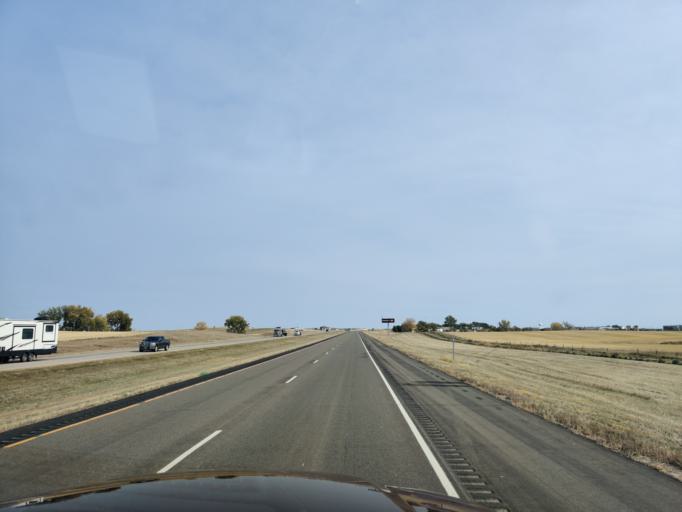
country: US
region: North Dakota
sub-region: Stark County
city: Dickinson
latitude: 46.8930
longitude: -102.7561
